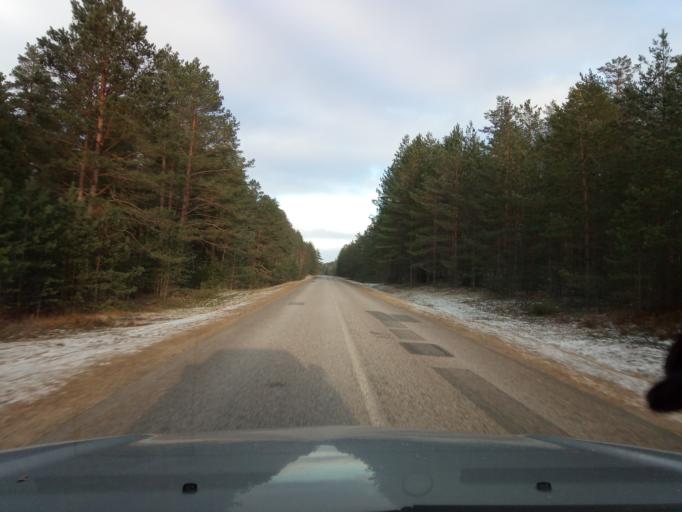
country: LT
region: Alytaus apskritis
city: Varena
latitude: 54.0957
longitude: 24.4213
